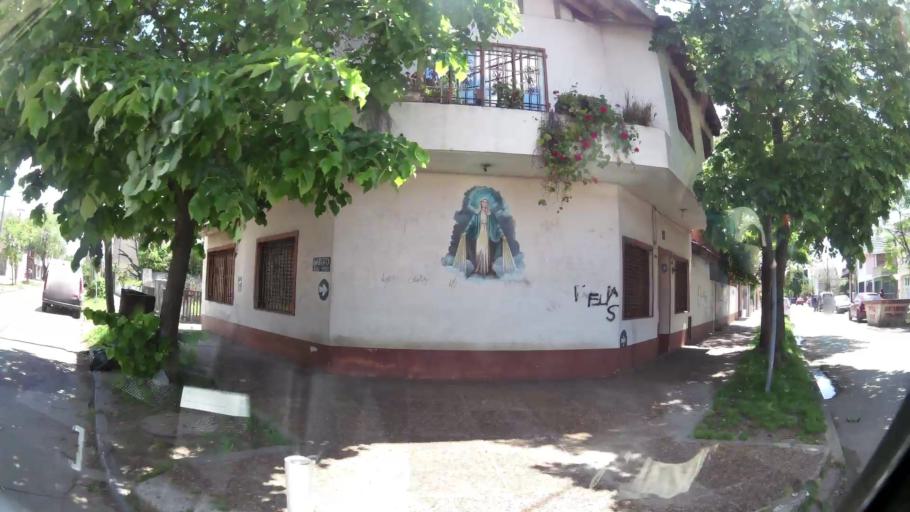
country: AR
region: Buenos Aires
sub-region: Partido de Lanus
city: Lanus
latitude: -34.7246
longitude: -58.4114
